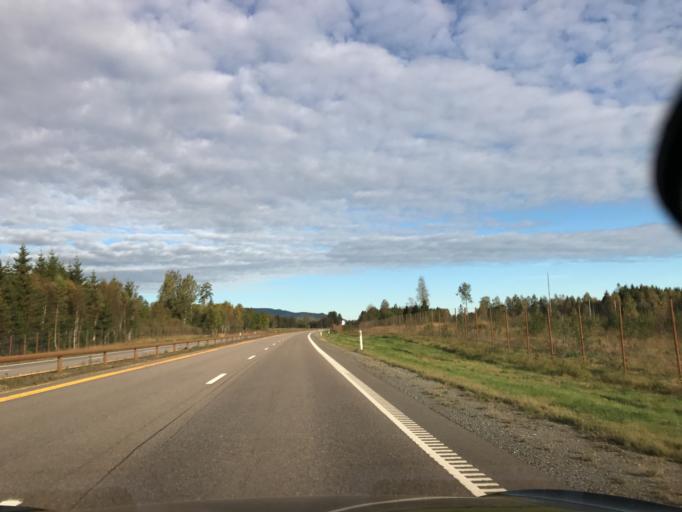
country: NO
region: Akershus
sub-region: Eidsvoll
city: Eidsvoll
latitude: 60.3592
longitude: 11.2052
